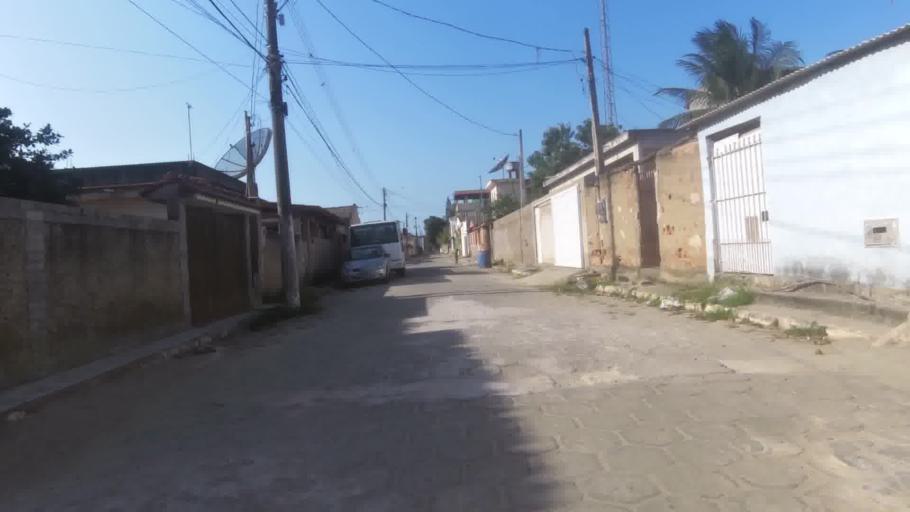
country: BR
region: Espirito Santo
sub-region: Itapemirim
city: Itapemirim
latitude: -21.0094
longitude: -40.8137
